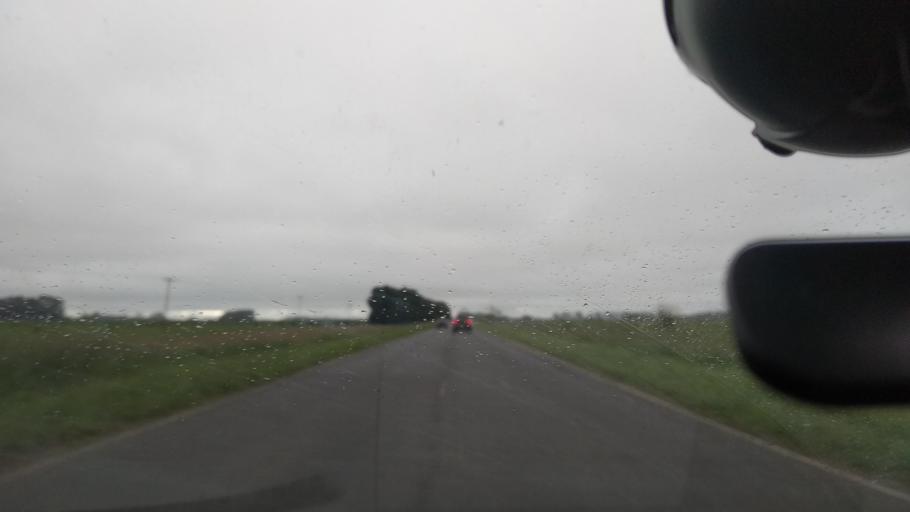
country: AR
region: Buenos Aires
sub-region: Partido de Magdalena
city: Magdalena
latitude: -35.2058
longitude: -57.7667
